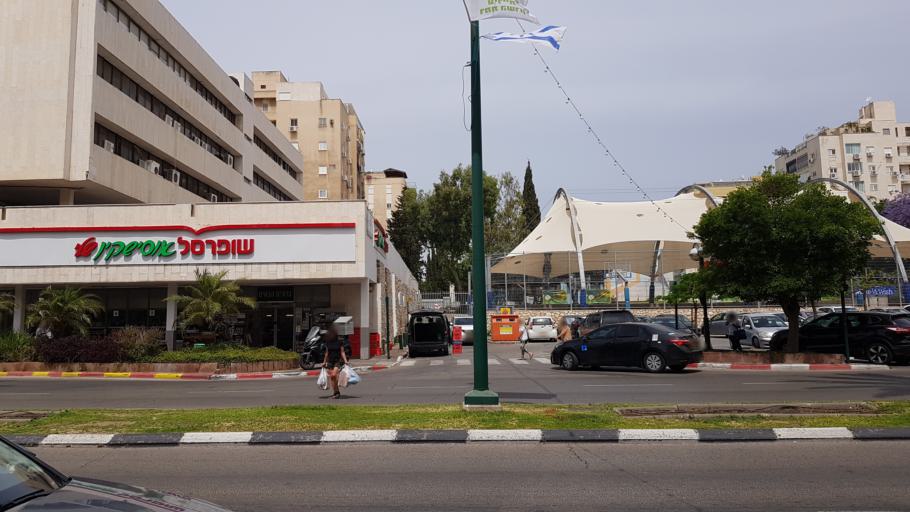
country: IL
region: Tel Aviv
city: Ramat HaSharon
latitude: 32.1385
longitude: 34.8418
